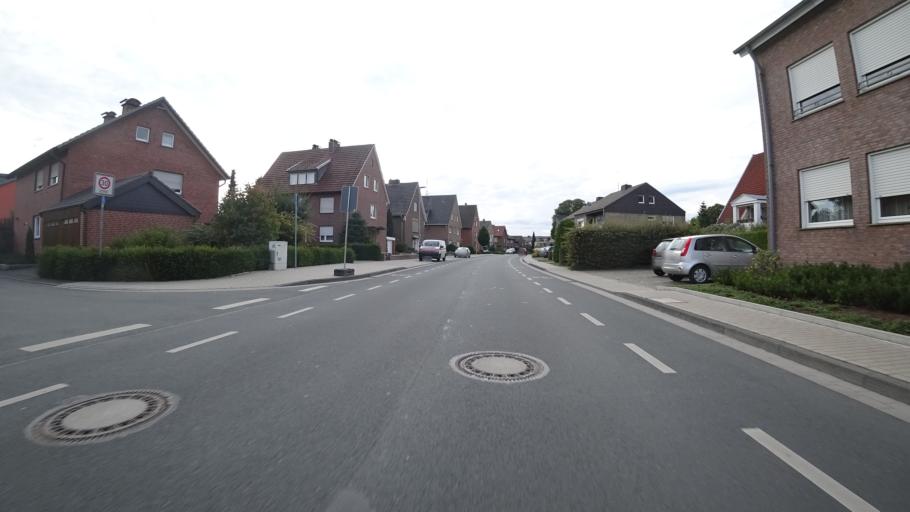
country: DE
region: North Rhine-Westphalia
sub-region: Regierungsbezirk Munster
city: Warendorf
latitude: 51.9475
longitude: 7.9981
